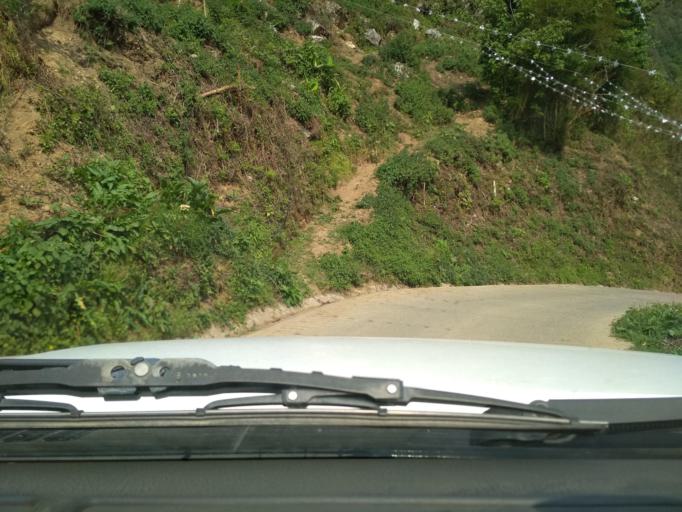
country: MX
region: Veracruz
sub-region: Camerino Z. Mendoza
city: Necoxtla
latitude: 18.7708
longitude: -97.1549
